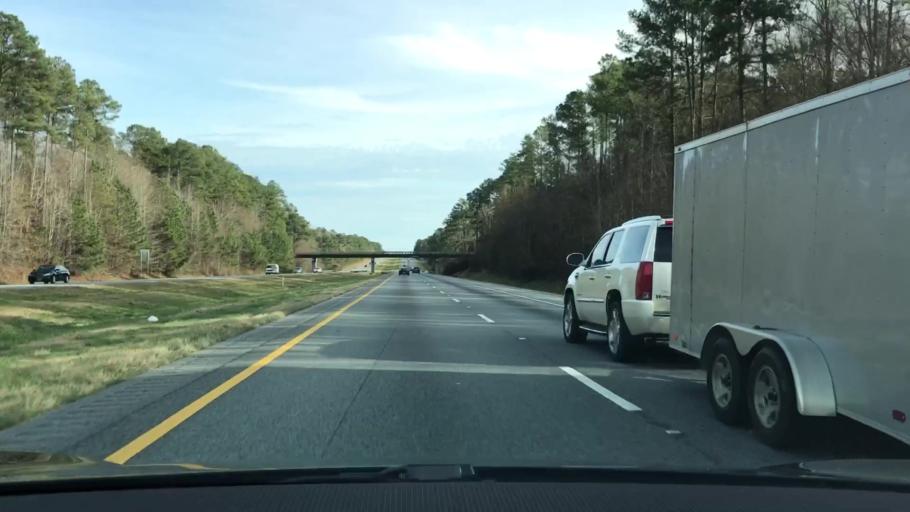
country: US
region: Georgia
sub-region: Morgan County
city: Madison
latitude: 33.5745
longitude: -83.5282
